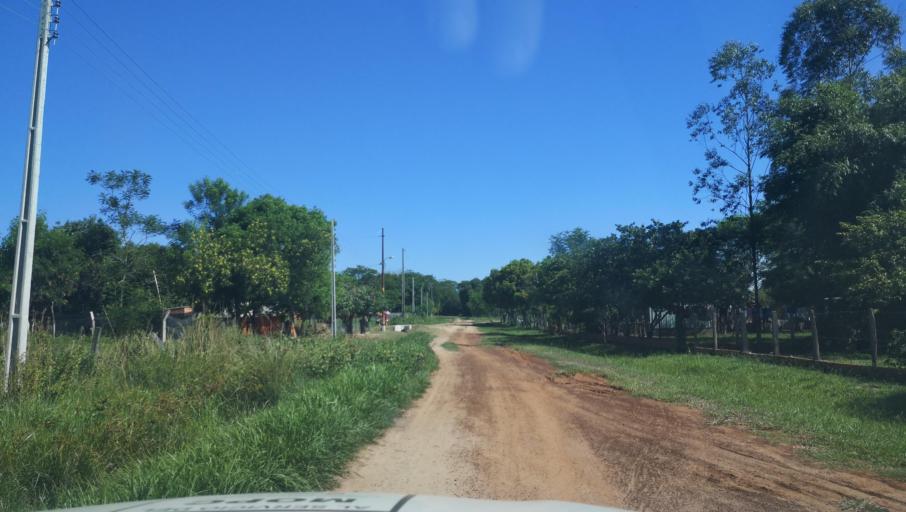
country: PY
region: Caaguazu
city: Carayao
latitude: -25.1998
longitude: -56.3939
